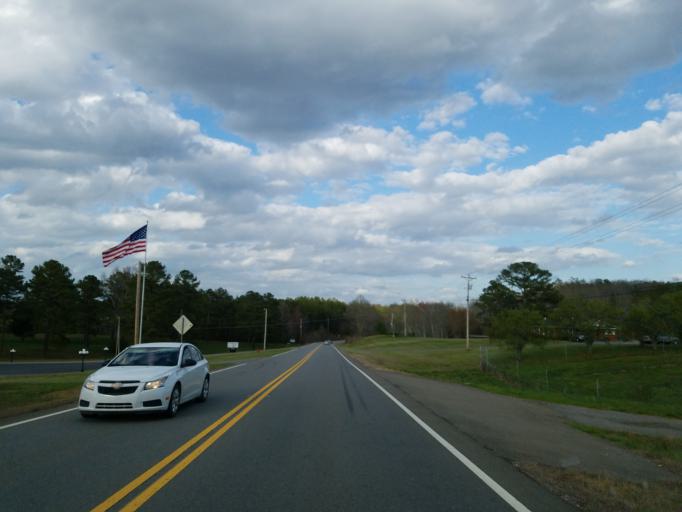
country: US
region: Georgia
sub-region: Bartow County
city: Rydal
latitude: 34.4496
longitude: -84.7653
